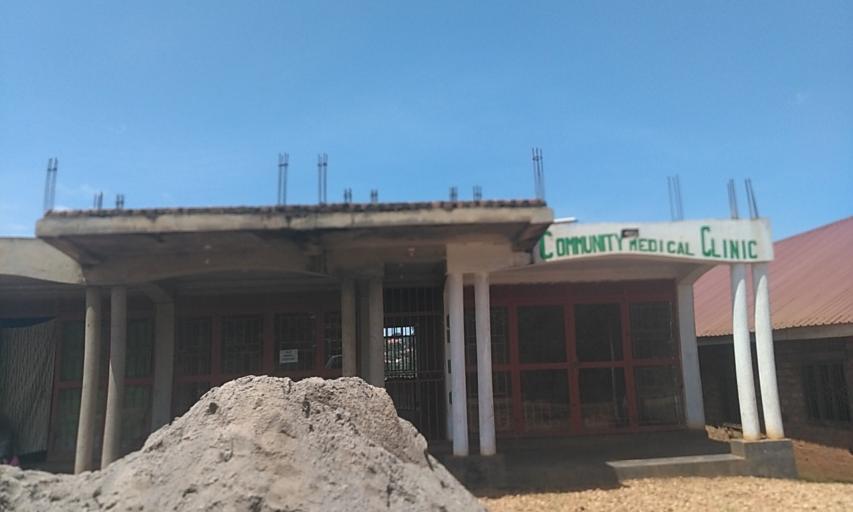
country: UG
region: Central Region
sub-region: Wakiso District
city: Wakiso
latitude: 0.4078
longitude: 32.4724
